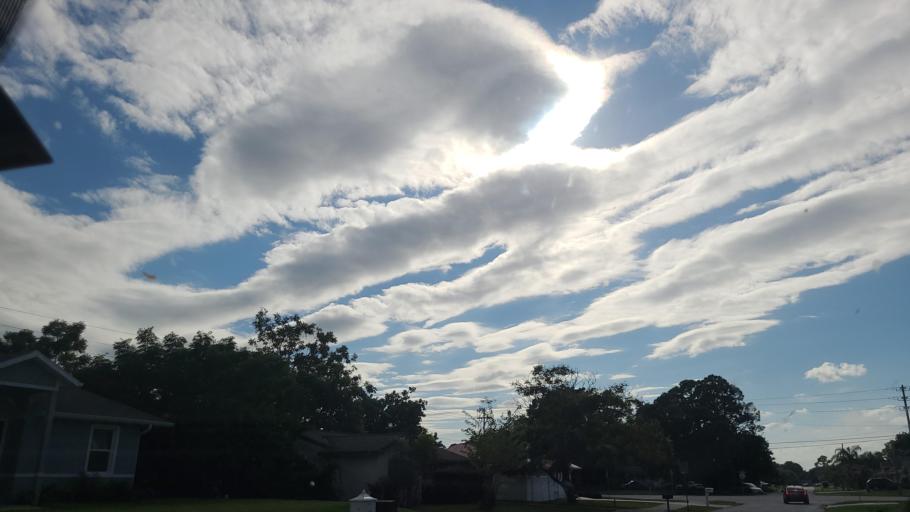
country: US
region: Florida
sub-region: Brevard County
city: Palm Bay
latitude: 27.9775
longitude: -80.6478
